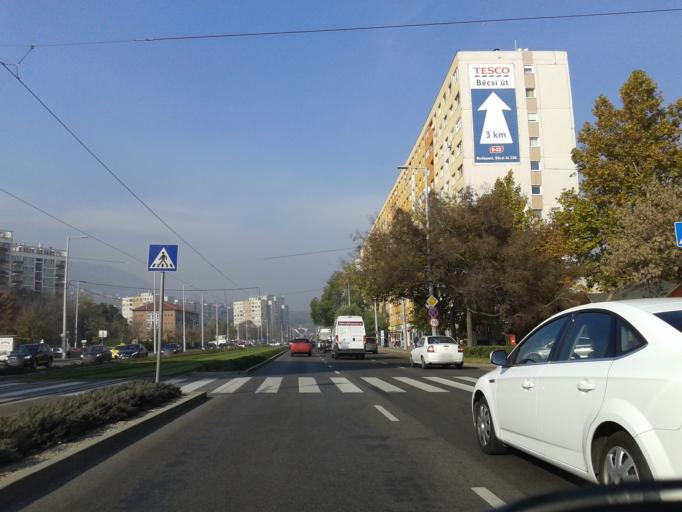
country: HU
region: Budapest
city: Budapest III. keruelet
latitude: 47.5433
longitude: 19.0371
